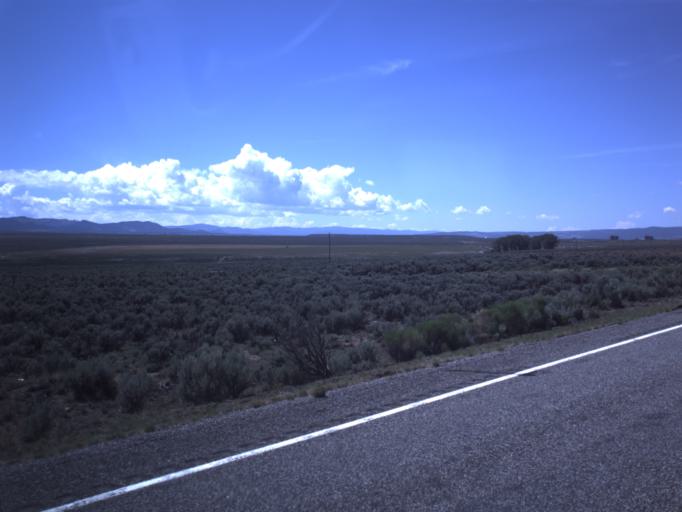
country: US
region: Utah
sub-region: Garfield County
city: Panguitch
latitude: 37.9908
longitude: -112.3927
